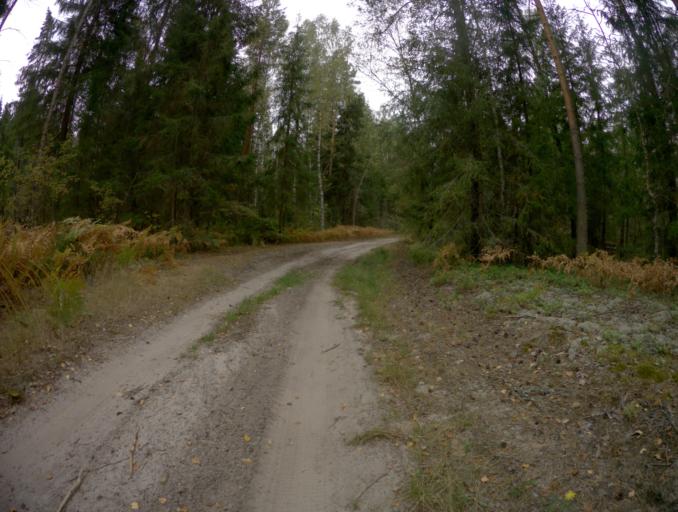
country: RU
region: Vladimir
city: Ivanishchi
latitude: 55.8513
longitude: 40.3592
